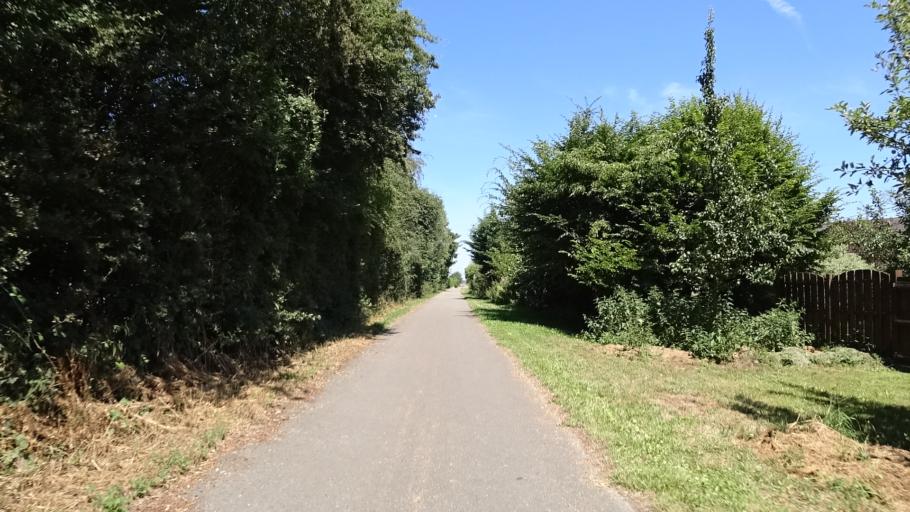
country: BE
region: Wallonia
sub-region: Province de Namur
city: Gembloux
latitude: 50.5929
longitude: 4.7284
